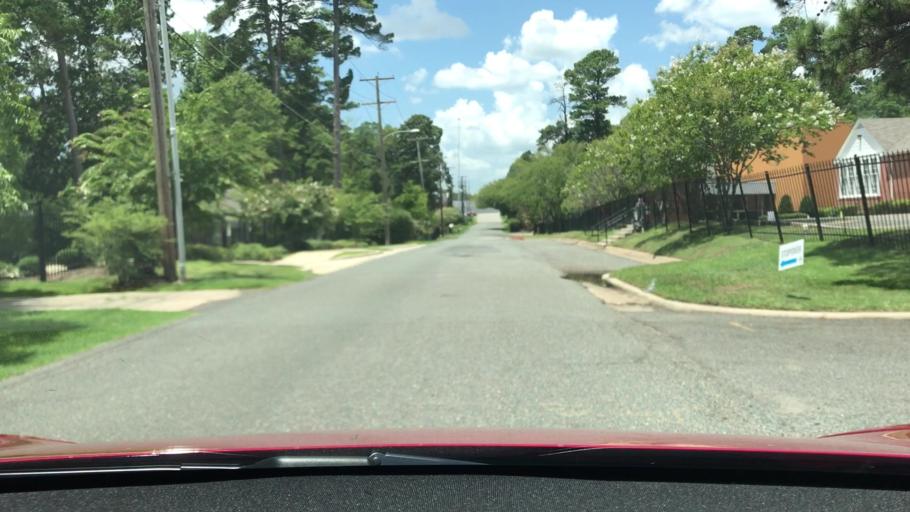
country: US
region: Louisiana
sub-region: Bossier Parish
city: Bossier City
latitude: 32.4565
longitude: -93.7515
